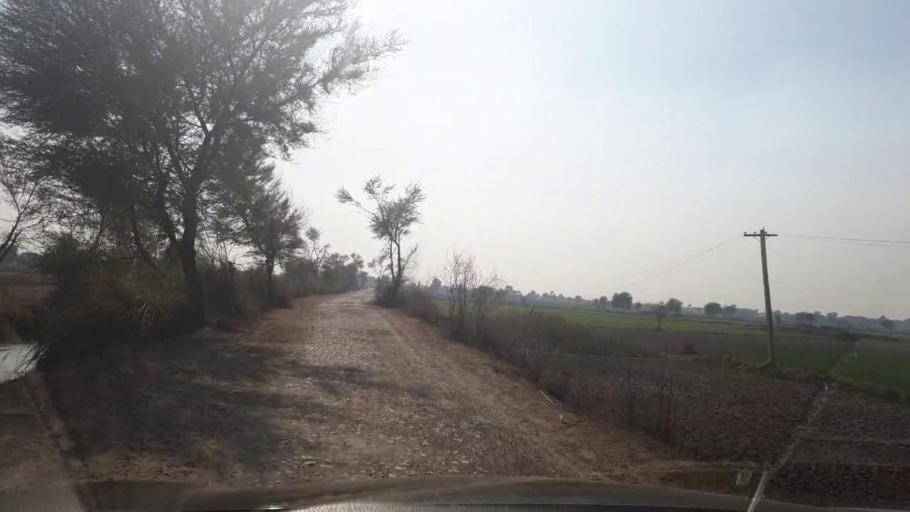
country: PK
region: Sindh
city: Khairpur
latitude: 28.1259
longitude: 69.6441
